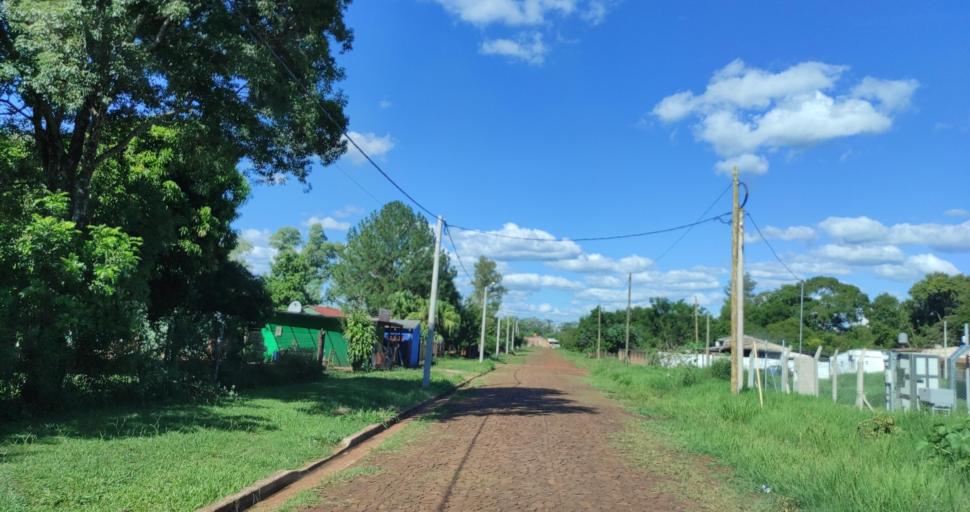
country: AR
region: Misiones
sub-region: Departamento de Candelaria
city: Candelaria
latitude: -27.4602
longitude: -55.7367
